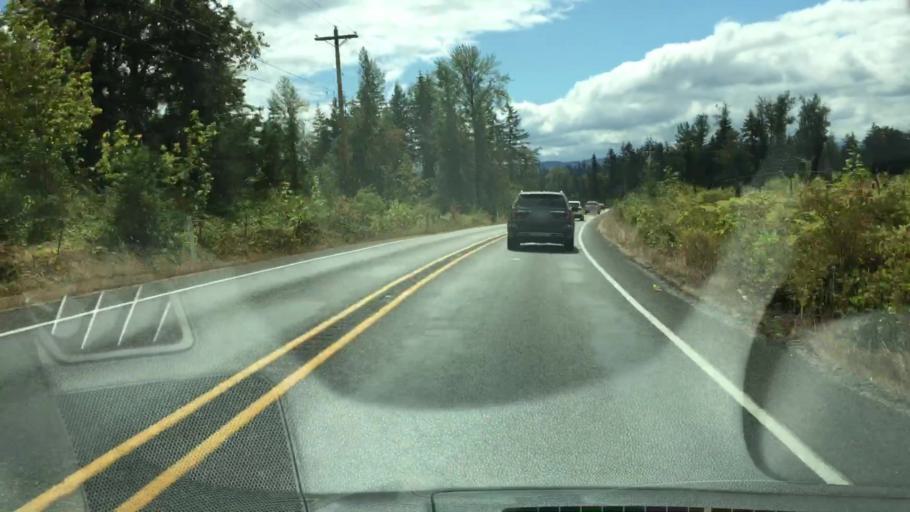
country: US
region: Washington
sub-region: Pierce County
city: Eatonville
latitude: 46.8925
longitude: -122.2980
